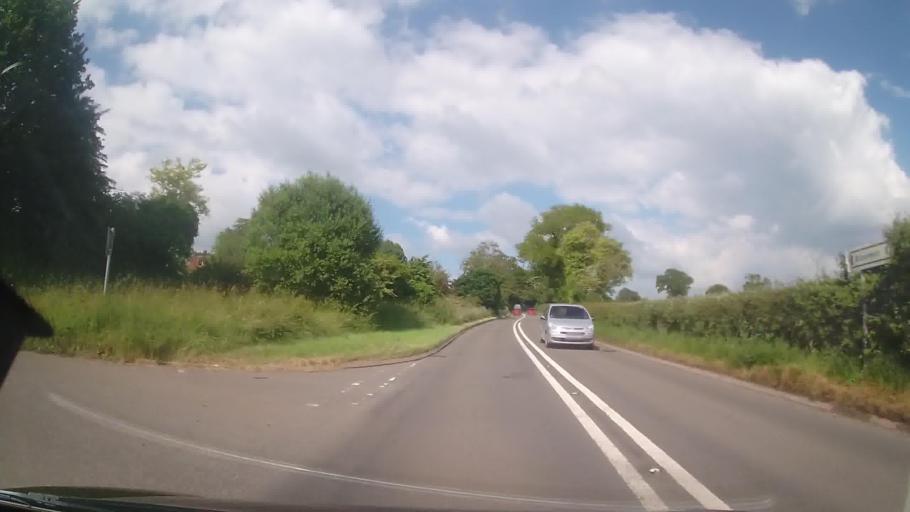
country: GB
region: England
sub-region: Shropshire
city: Whittington
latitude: 52.8894
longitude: -2.9570
